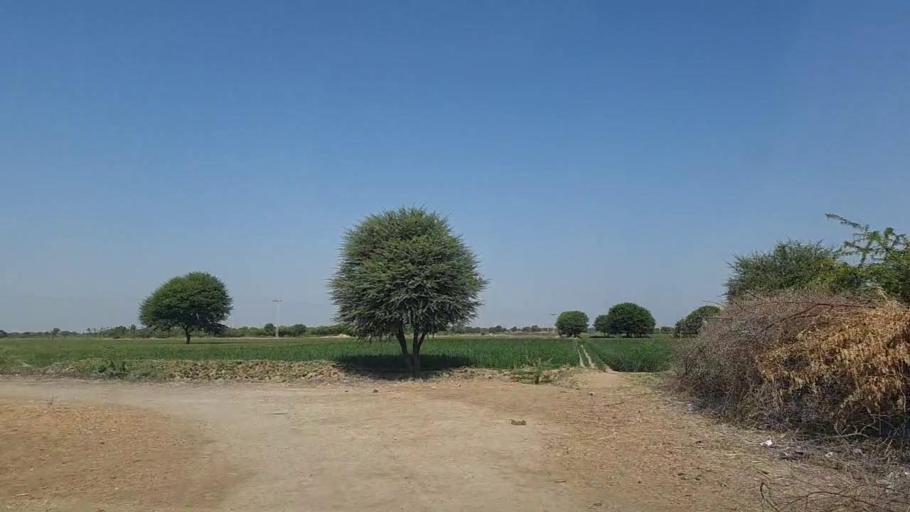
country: PK
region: Sindh
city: Samaro
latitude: 25.2494
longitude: 69.4484
